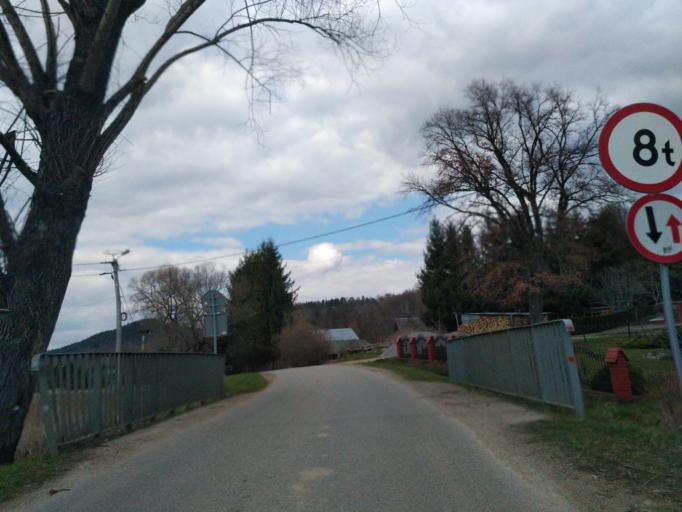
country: PL
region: Subcarpathian Voivodeship
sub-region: Powiat sanocki
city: Tyrawa Woloska
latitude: 49.6559
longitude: 22.3022
